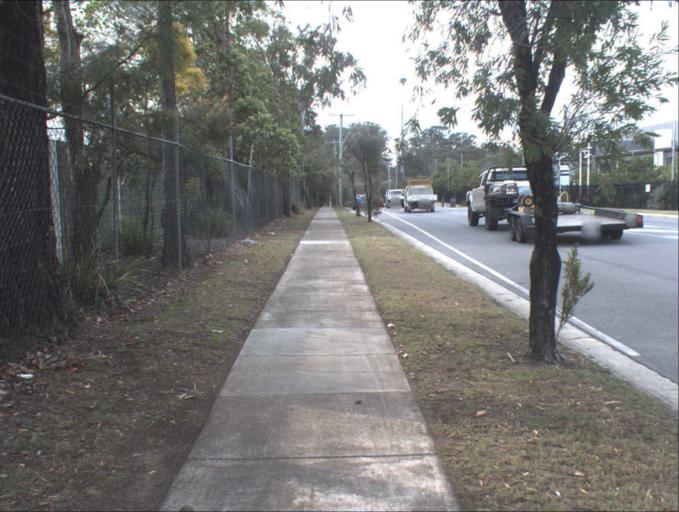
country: AU
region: Queensland
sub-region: Logan
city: Waterford West
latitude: -27.6661
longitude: 153.1239
